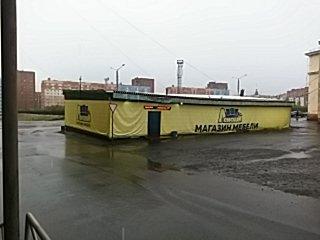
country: RU
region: Krasnoyarskiy
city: Norilsk
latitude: 69.3452
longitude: 88.2122
